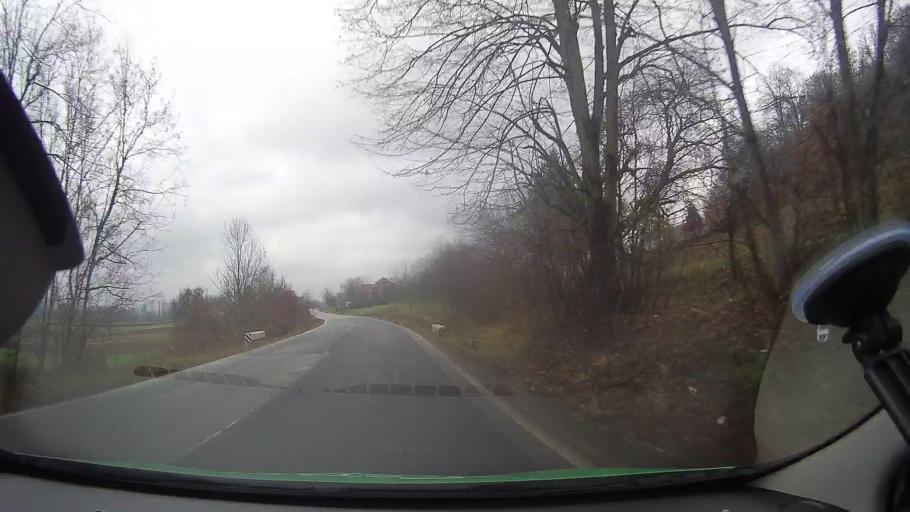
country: RO
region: Arad
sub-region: Comuna Buteni
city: Buteni
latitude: 46.2994
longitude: 22.1695
